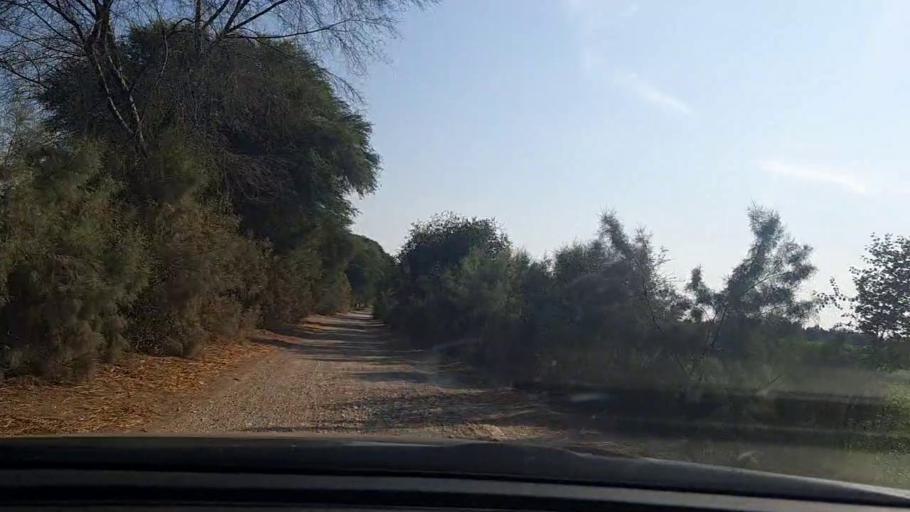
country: PK
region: Sindh
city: Sehwan
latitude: 26.3059
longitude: 68.0014
